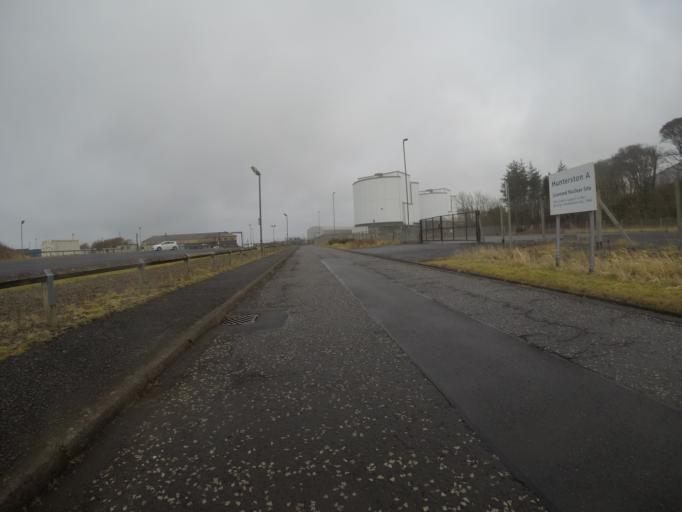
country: GB
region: Scotland
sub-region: North Ayrshire
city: Millport
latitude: 55.7181
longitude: -4.9005
